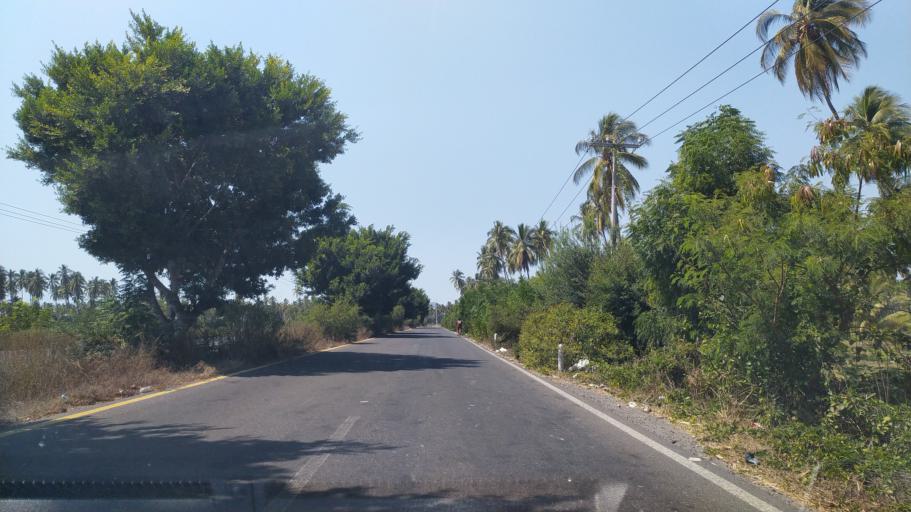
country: MX
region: Colima
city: Tecoman
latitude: 18.9332
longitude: -103.8641
